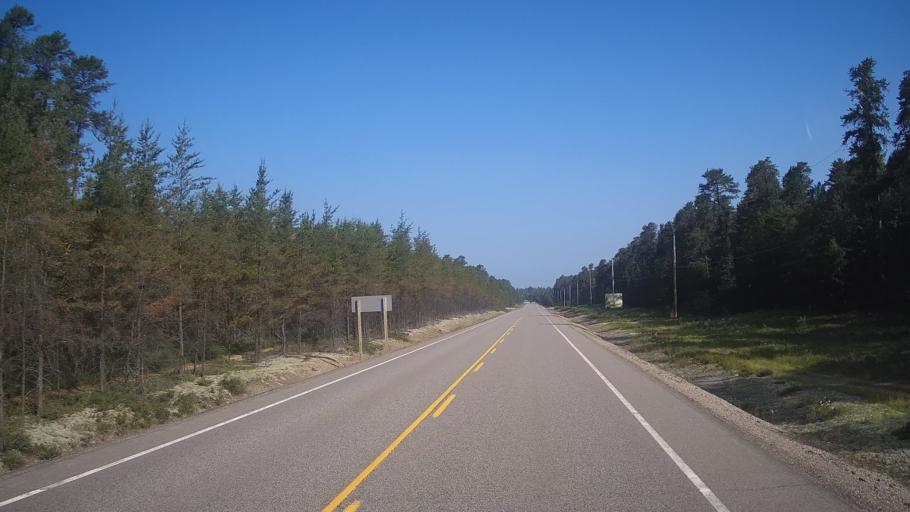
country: CA
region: Ontario
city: Rayside-Balfour
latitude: 46.7223
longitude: -81.5714
